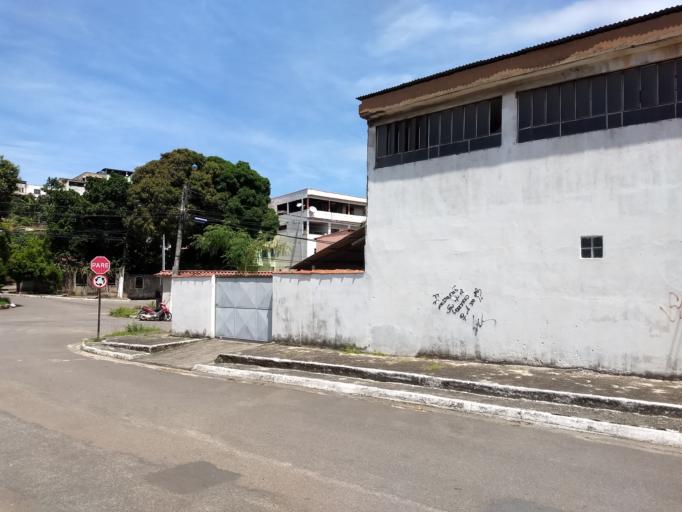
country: BR
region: Espirito Santo
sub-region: Vila Velha
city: Vila Velha
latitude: -20.3452
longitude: -40.3050
